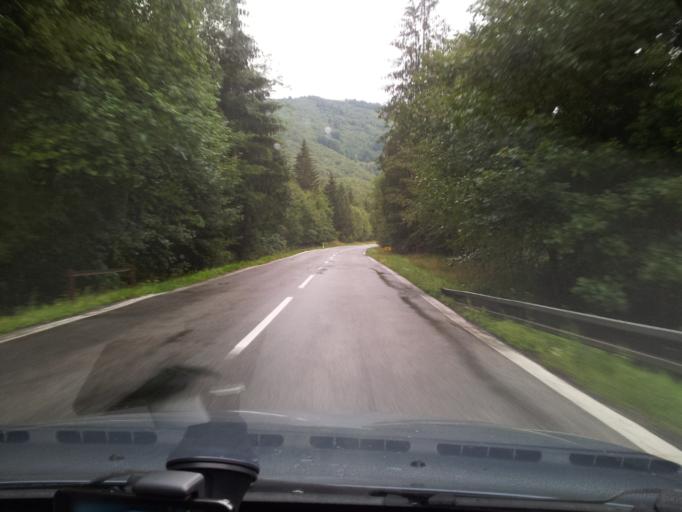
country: SK
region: Banskobystricky
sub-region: Okres Banska Bystrica
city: Brezno
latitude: 48.8718
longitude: 19.6534
